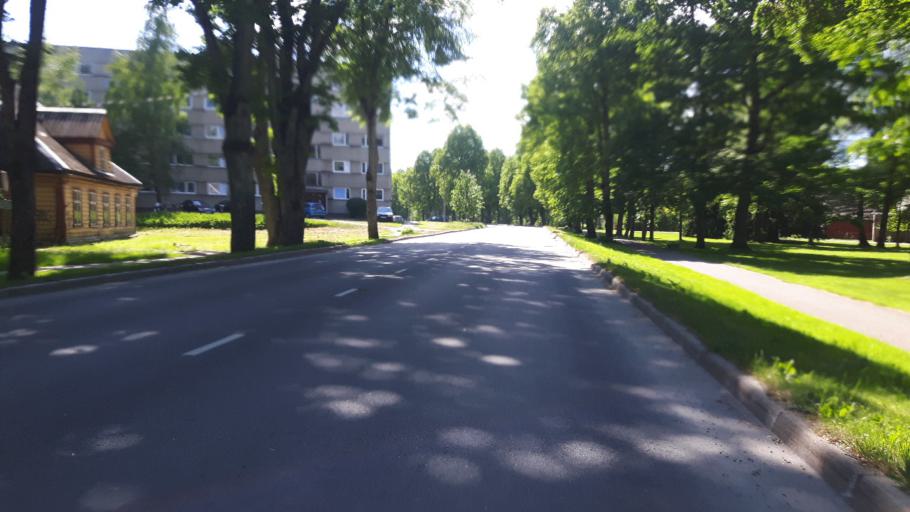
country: EE
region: Paernumaa
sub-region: Sindi linn
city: Sindi
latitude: 58.4071
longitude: 24.6559
